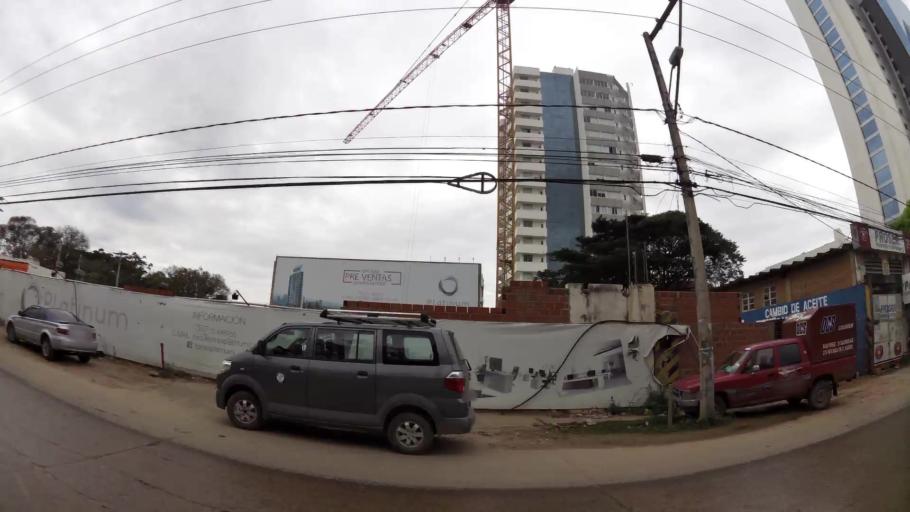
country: BO
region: Santa Cruz
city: Santa Cruz de la Sierra
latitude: -17.7547
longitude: -63.1976
